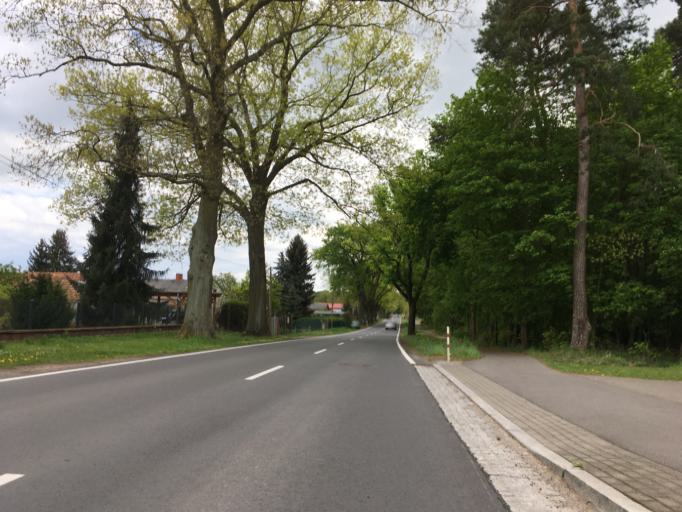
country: DE
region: Brandenburg
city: Bernau bei Berlin
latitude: 52.6383
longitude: 13.6112
